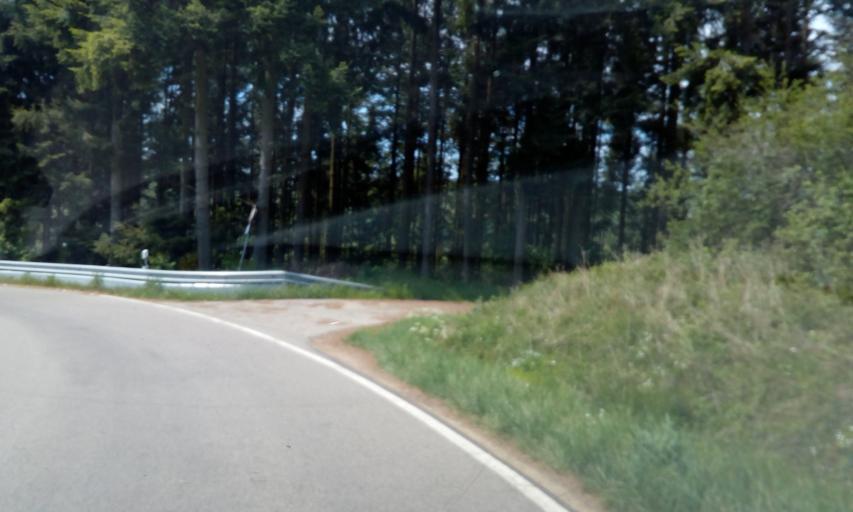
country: DE
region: Rheinland-Pfalz
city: Keppeshausen
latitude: 49.9693
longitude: 6.1742
